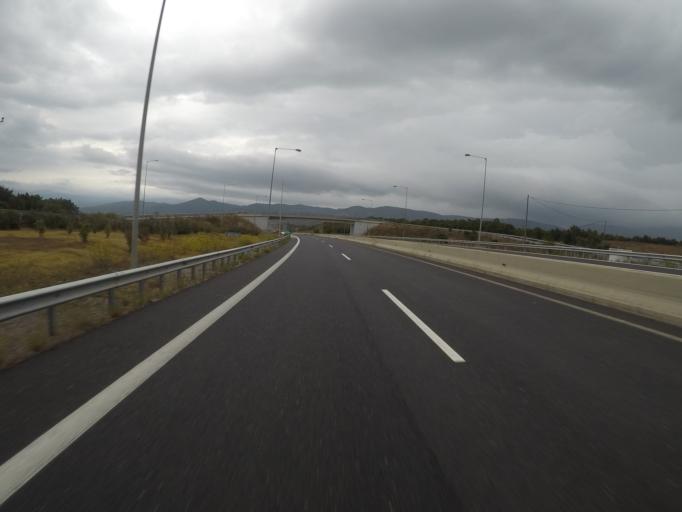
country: GR
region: Peloponnese
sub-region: Nomos Arkadias
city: Megalopoli
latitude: 37.3619
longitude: 22.1492
